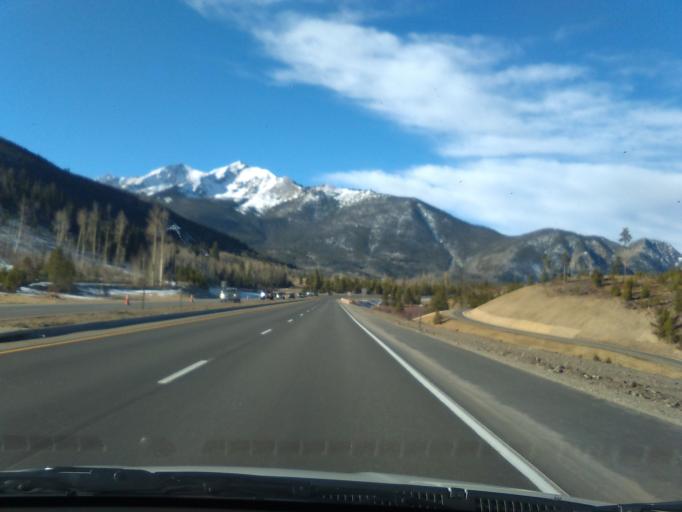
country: US
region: Colorado
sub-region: Summit County
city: Frisco
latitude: 39.5739
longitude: -106.0648
